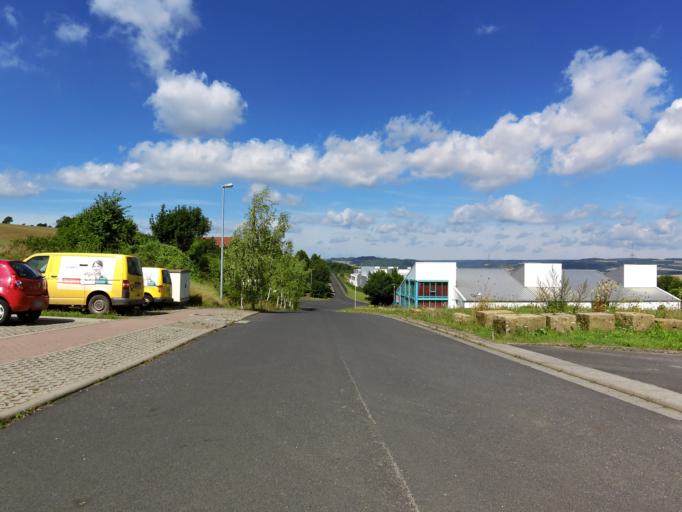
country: DE
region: Thuringia
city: Krauthausen
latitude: 51.0111
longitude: 10.2512
